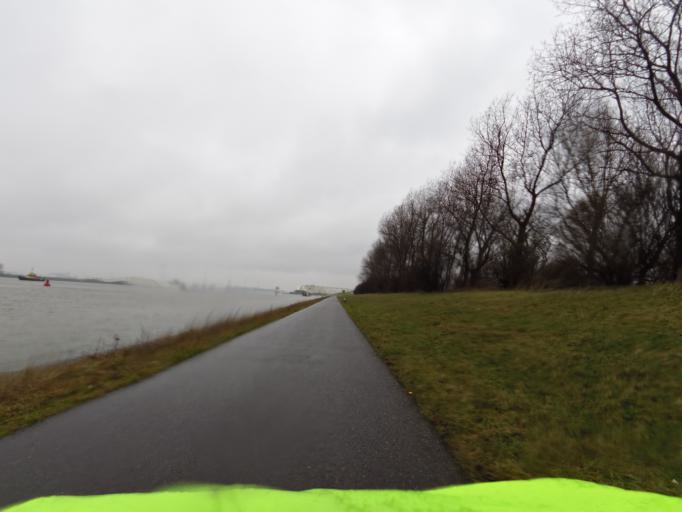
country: NL
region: South Holland
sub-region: Gemeente Westland
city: Maasdijk
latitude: 51.9517
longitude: 4.1761
